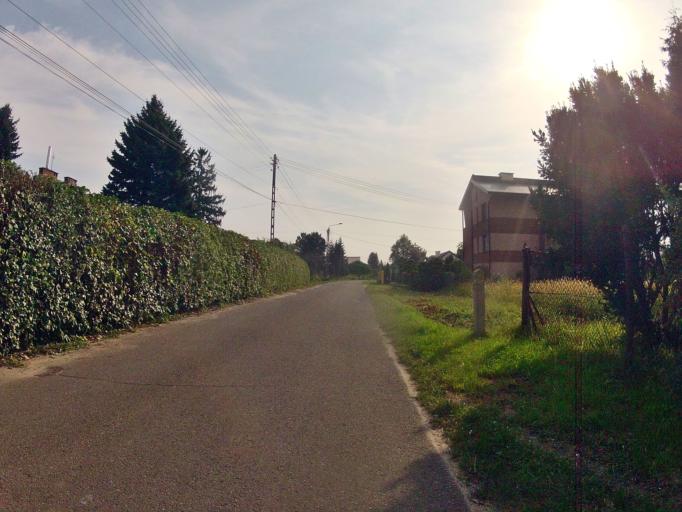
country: PL
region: Subcarpathian Voivodeship
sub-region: Powiat jasielski
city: Jaslo
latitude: 49.7384
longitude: 21.4501
